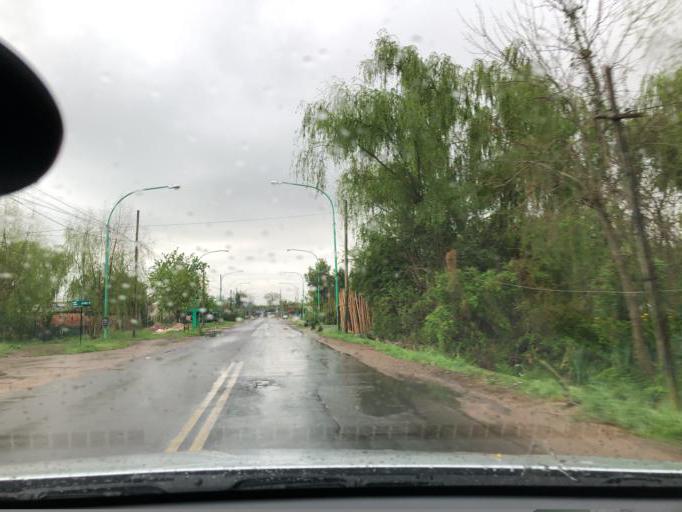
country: AR
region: Buenos Aires
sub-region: Partido de Ensenada
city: Ensenada
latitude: -34.8410
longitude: -57.9357
